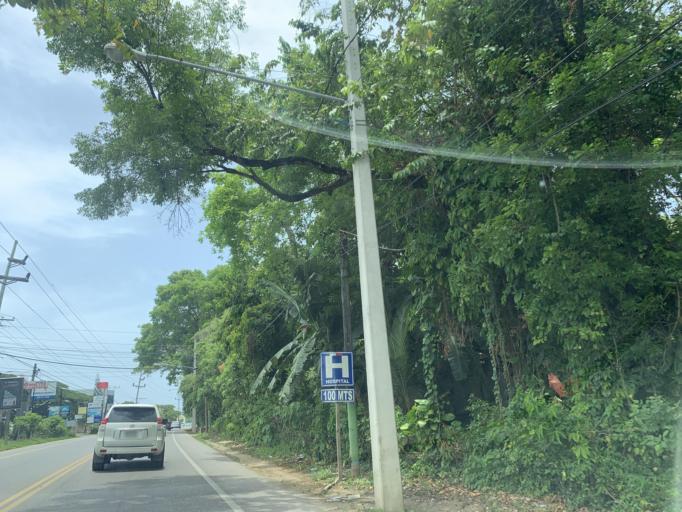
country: DO
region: Puerto Plata
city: Cabarete
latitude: 19.7680
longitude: -70.5059
